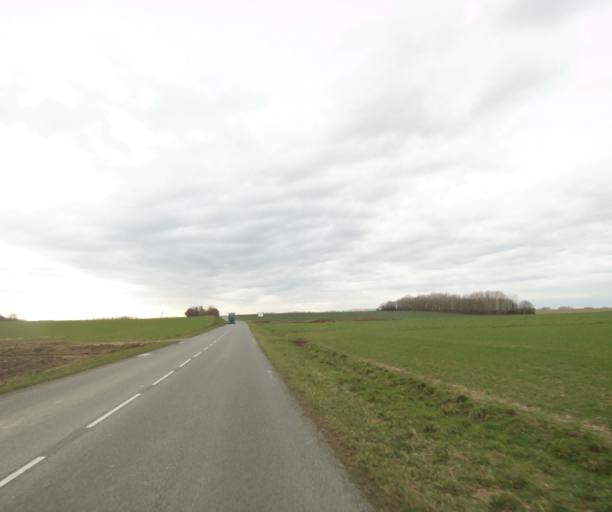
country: FR
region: Nord-Pas-de-Calais
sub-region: Departement du Nord
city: Sebourg
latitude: 50.3327
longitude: 3.6356
